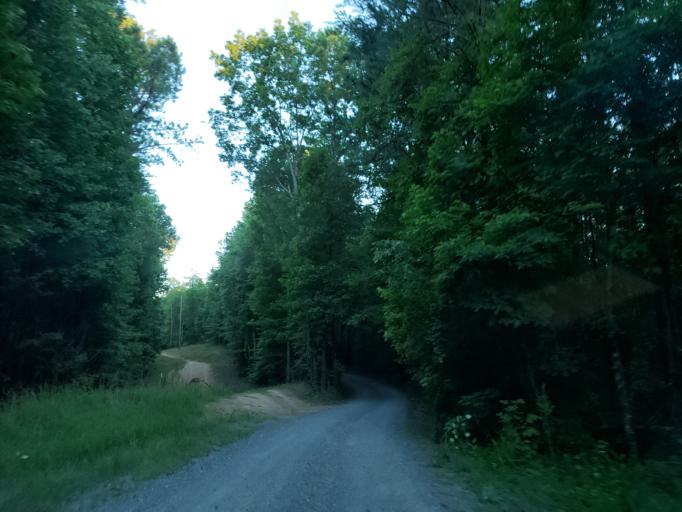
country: US
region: Georgia
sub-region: Bartow County
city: Euharlee
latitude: 34.0884
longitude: -84.8686
